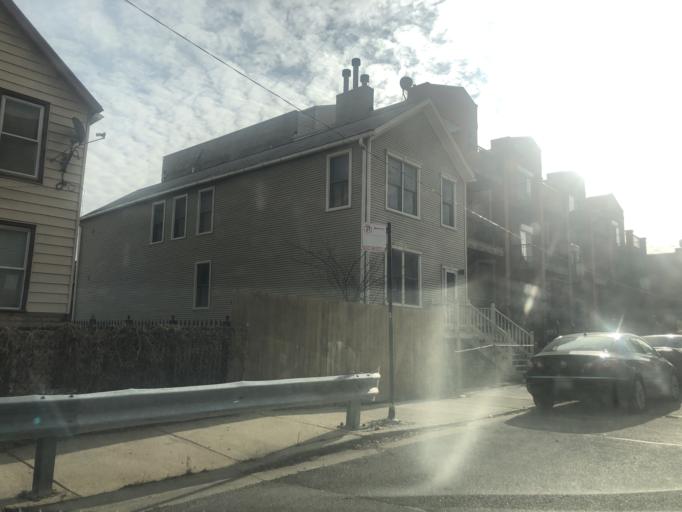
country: US
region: Illinois
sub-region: Cook County
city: Chicago
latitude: 41.8970
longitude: -87.6638
